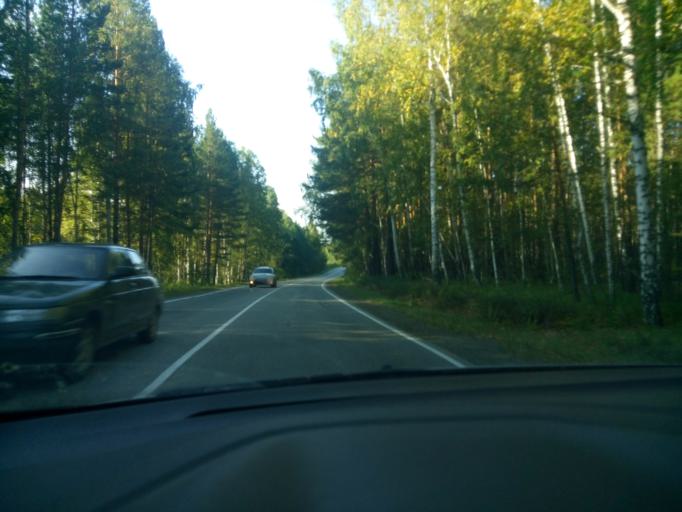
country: RU
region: Chelyabinsk
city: Ozersk
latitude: 55.8449
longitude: 60.6555
